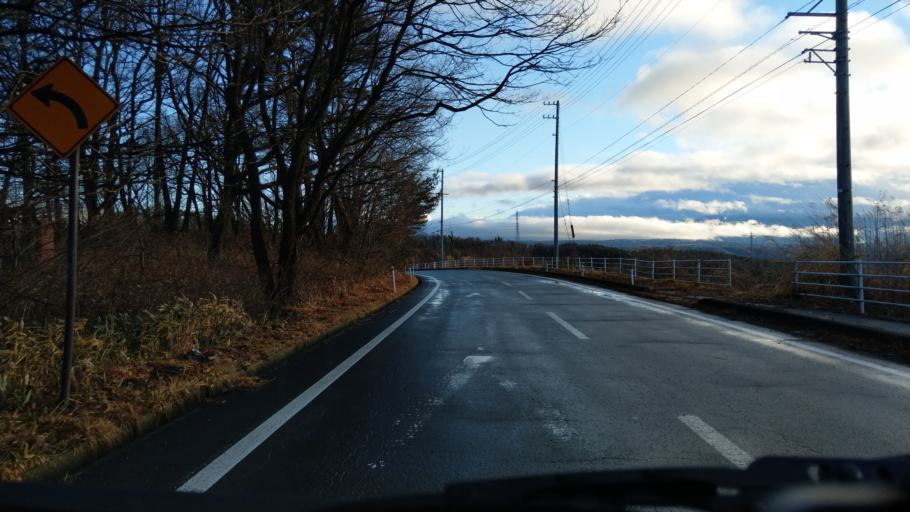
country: JP
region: Nagano
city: Komoro
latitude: 36.3002
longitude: 138.4115
